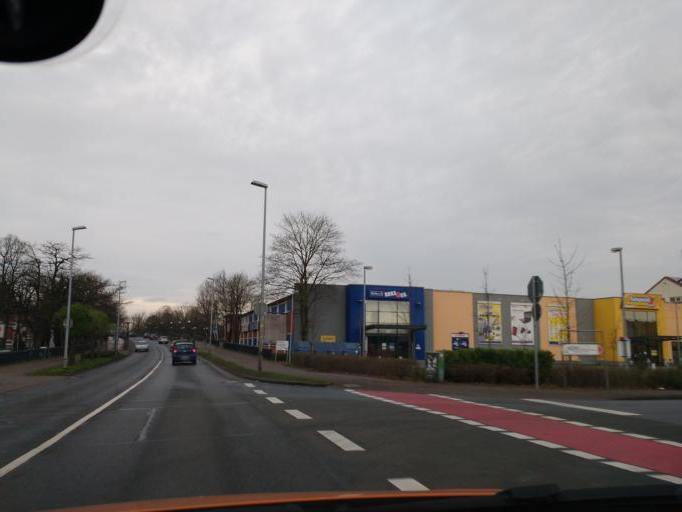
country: DE
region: Lower Saxony
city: Oldenburg
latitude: 53.1368
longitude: 8.2270
